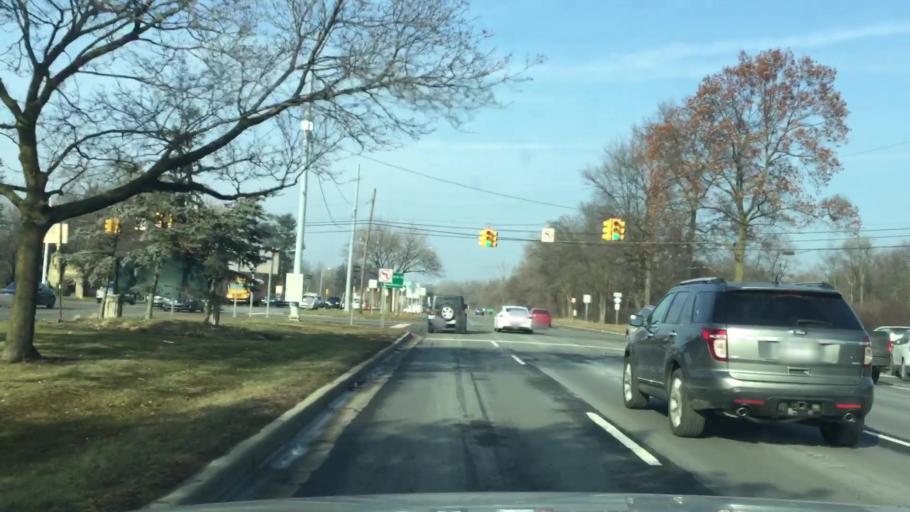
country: US
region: Michigan
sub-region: Oakland County
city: Birmingham
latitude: 42.5598
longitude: -83.2238
